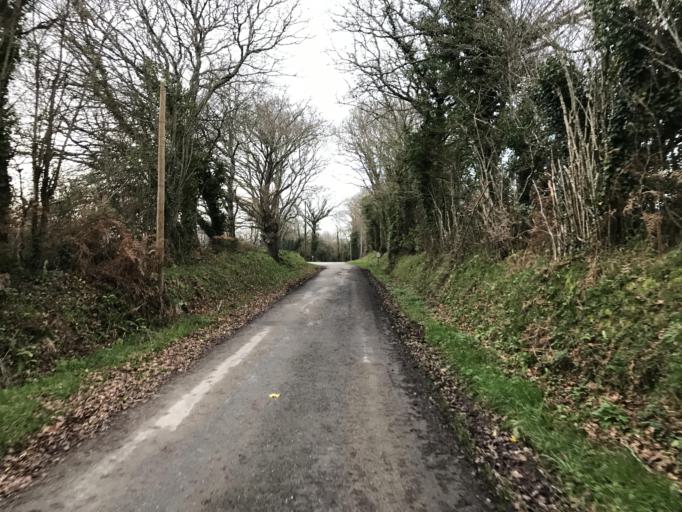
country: FR
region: Brittany
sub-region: Departement du Finistere
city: Loperhet
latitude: 48.3561
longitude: -4.2924
